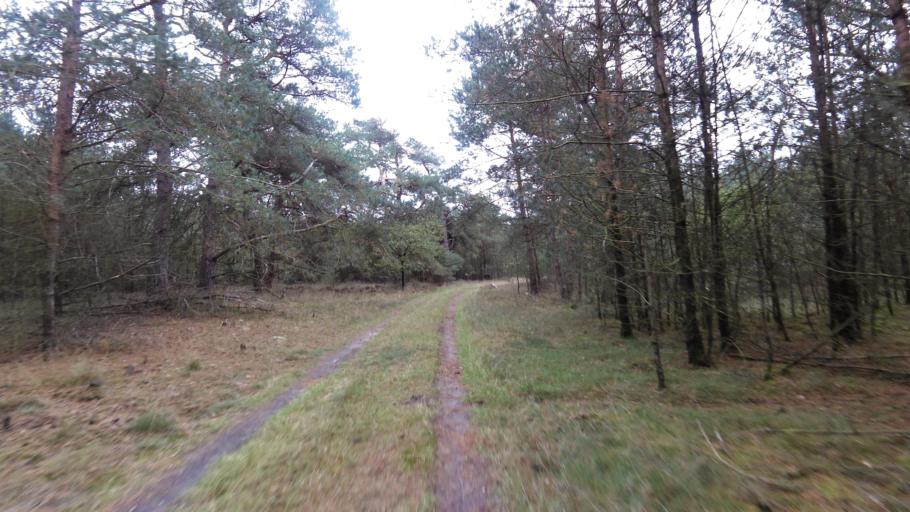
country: NL
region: Gelderland
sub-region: Gemeente Barneveld
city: Garderen
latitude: 52.1961
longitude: 5.7615
